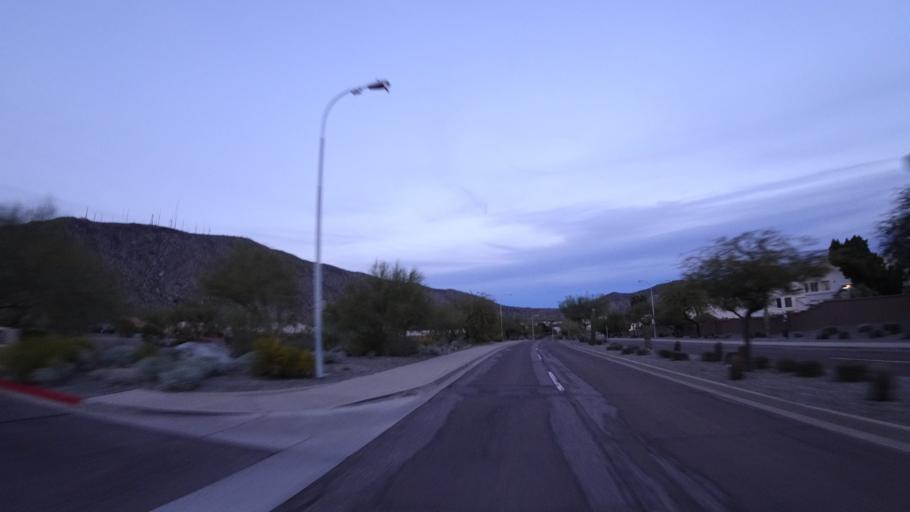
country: US
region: Arizona
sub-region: Maricopa County
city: Laveen
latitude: 33.3173
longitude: -112.0662
